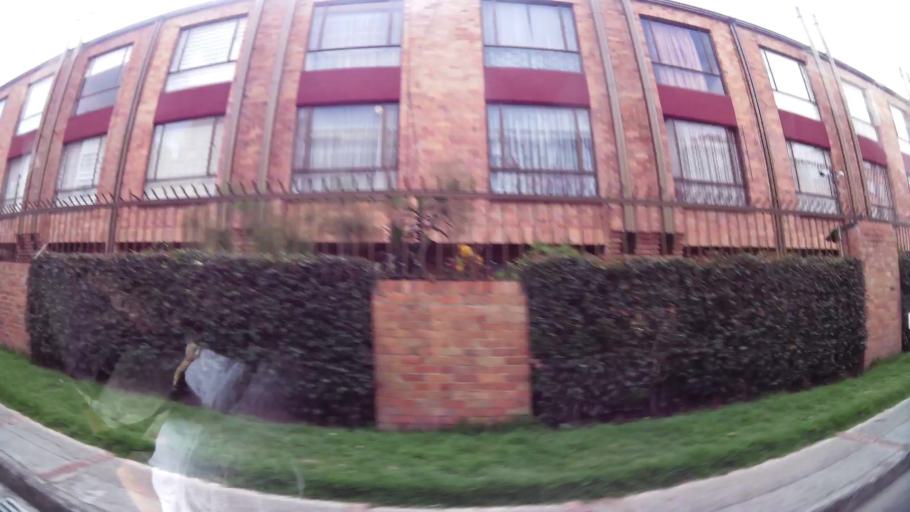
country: CO
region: Bogota D.C.
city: Barrio San Luis
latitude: 4.7290
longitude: -74.0313
